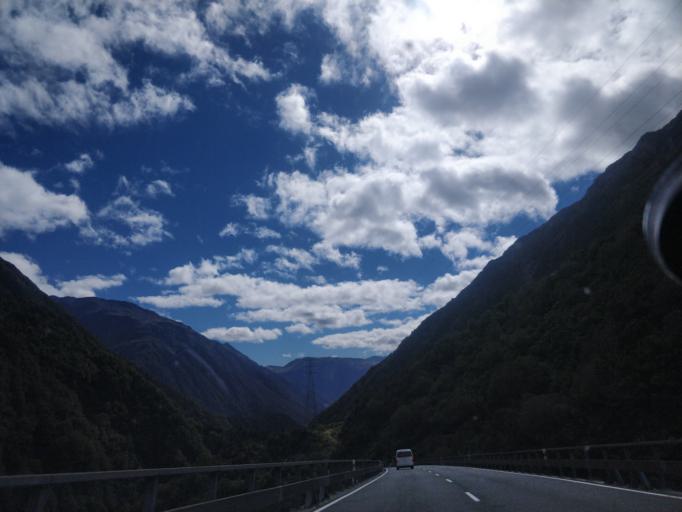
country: NZ
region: West Coast
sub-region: Grey District
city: Greymouth
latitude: -42.8855
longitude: 171.5558
